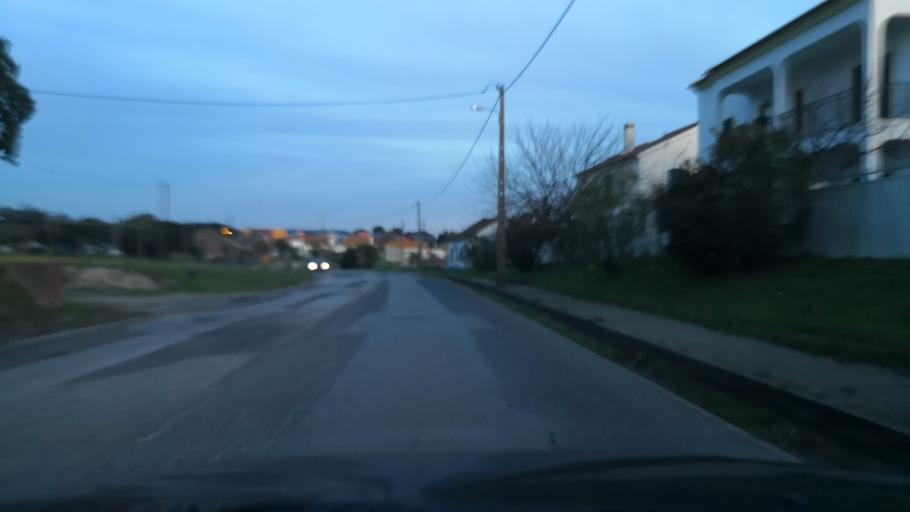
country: PT
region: Setubal
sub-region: Setubal
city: Setubal
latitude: 38.5235
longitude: -8.8333
